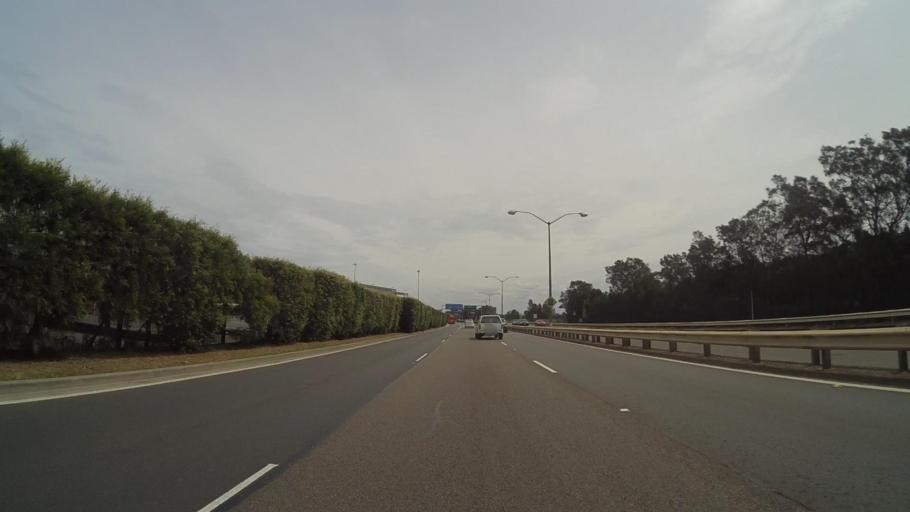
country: AU
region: New South Wales
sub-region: Rockdale
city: Arncliffe
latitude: -33.9283
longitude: 151.1675
